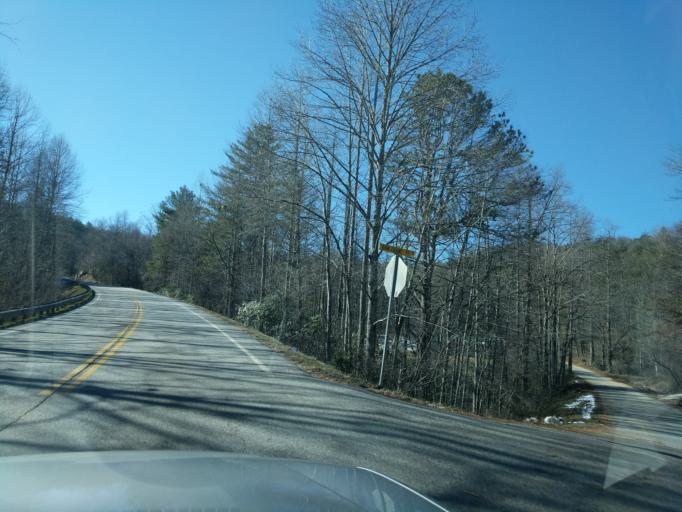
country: US
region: Georgia
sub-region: Rabun County
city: Clayton
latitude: 34.8747
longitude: -83.4529
